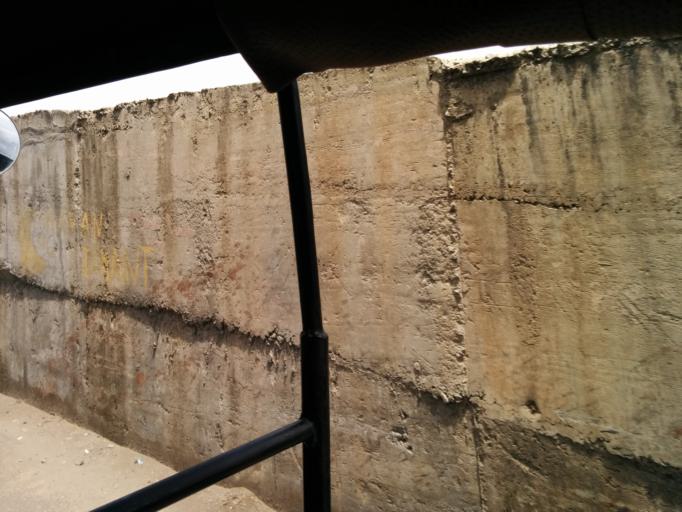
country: IN
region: Maharashtra
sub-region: Pune Division
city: Lohogaon
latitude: 18.5553
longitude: 73.9066
